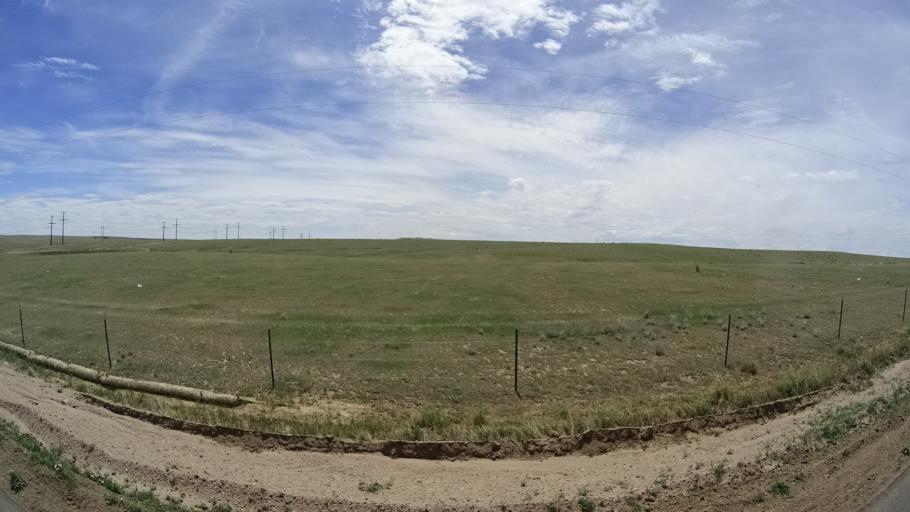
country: US
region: Colorado
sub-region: El Paso County
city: Fountain
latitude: 38.6940
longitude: -104.6324
